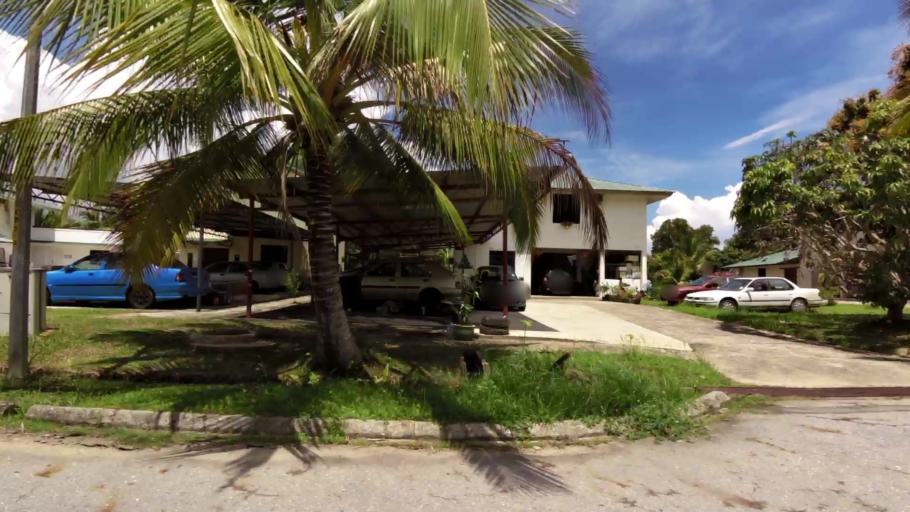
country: BN
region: Brunei and Muara
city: Bandar Seri Begawan
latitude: 4.9596
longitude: 114.9044
